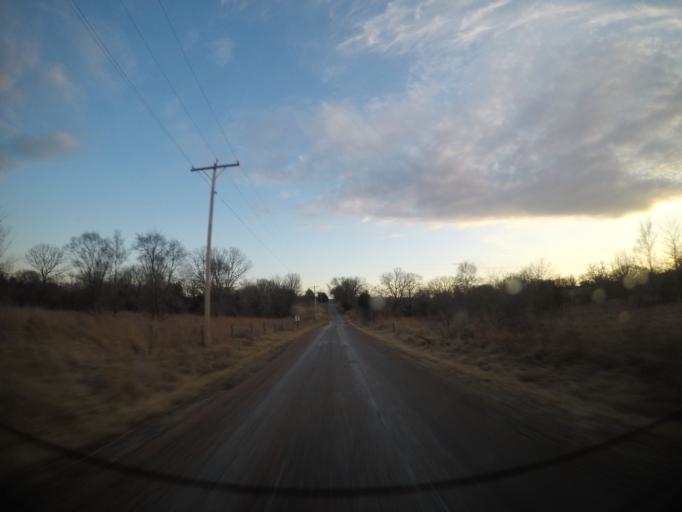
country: US
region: Kansas
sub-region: Wyandotte County
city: Bonner Springs
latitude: 39.0250
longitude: -94.9088
